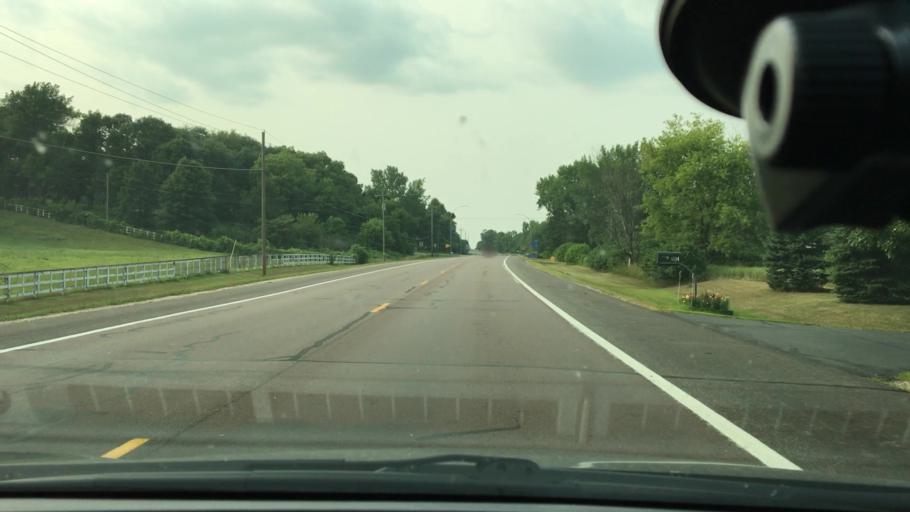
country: US
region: Minnesota
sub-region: Hennepin County
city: Dayton
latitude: 45.2506
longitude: -93.5362
